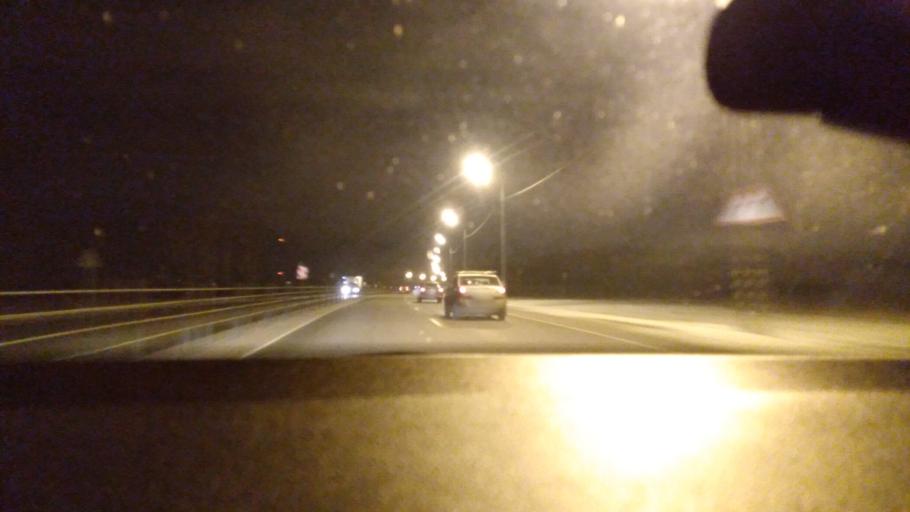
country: RU
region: Moskovskaya
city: Troitskoye
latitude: 55.3419
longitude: 38.4359
